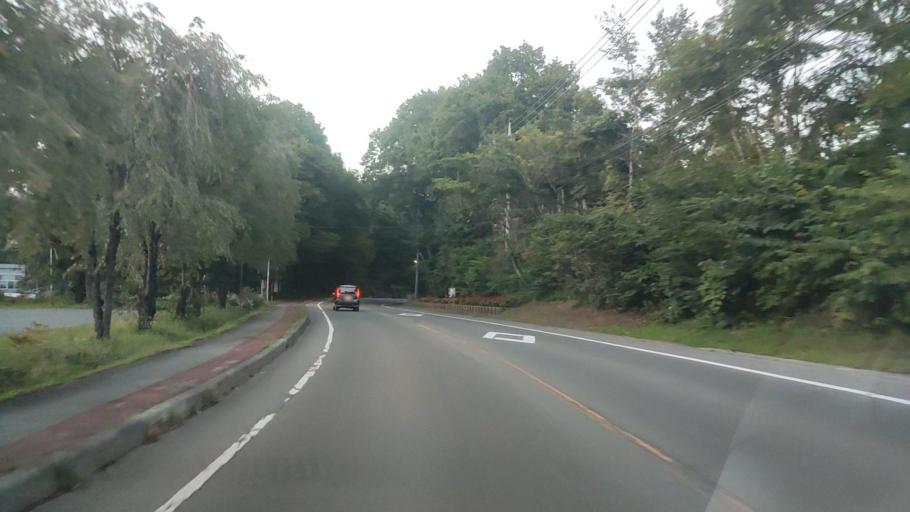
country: JP
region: Nagano
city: Komoro
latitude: 36.5018
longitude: 138.5898
